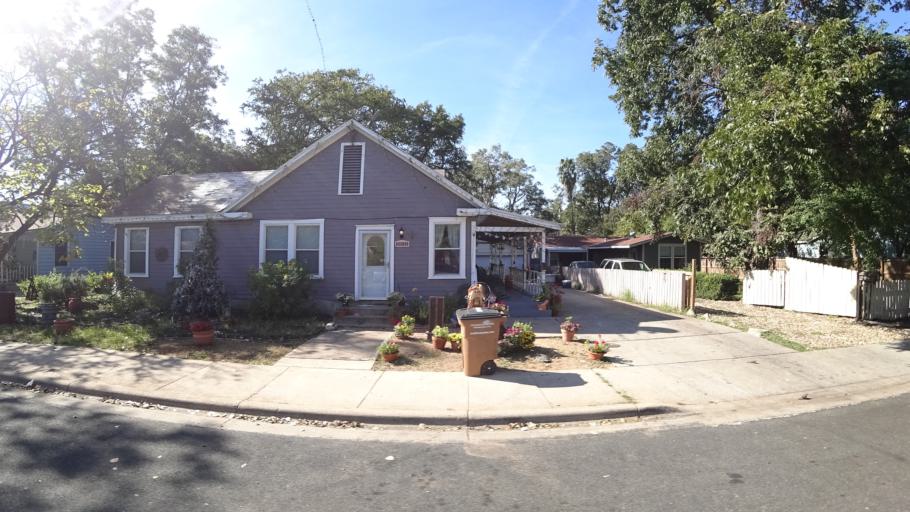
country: US
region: Texas
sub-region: Travis County
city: Austin
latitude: 30.2598
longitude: -97.6958
